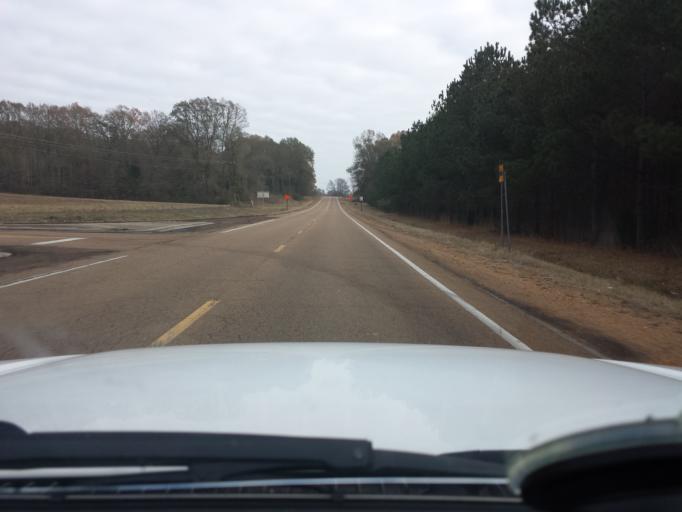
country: US
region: Mississippi
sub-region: Yazoo County
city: Yazoo City
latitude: 32.7922
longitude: -90.2081
